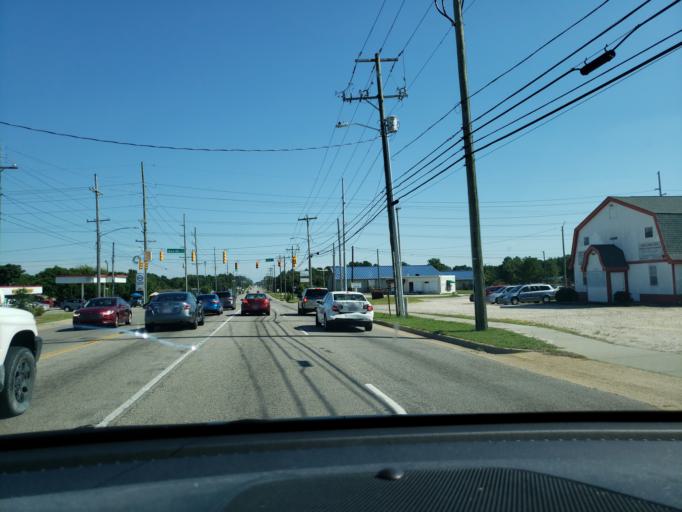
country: US
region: North Carolina
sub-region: Cumberland County
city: Spring Lake
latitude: 35.1121
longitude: -78.9282
